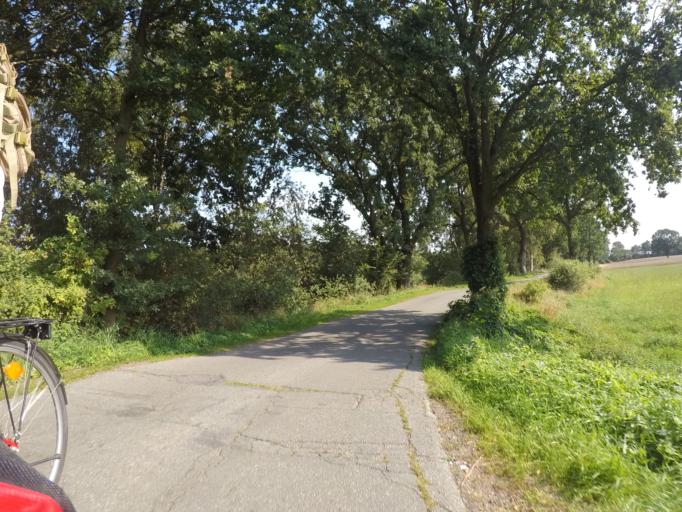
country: DE
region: Schleswig-Holstein
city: Seth
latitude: 53.8727
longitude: 10.1727
